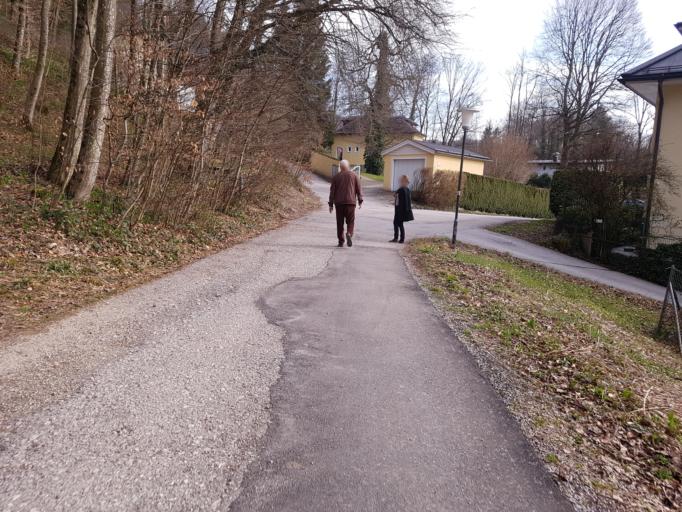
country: AT
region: Salzburg
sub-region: Politischer Bezirk Salzburg-Umgebung
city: Elsbethen
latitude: 47.7903
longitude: 13.0888
